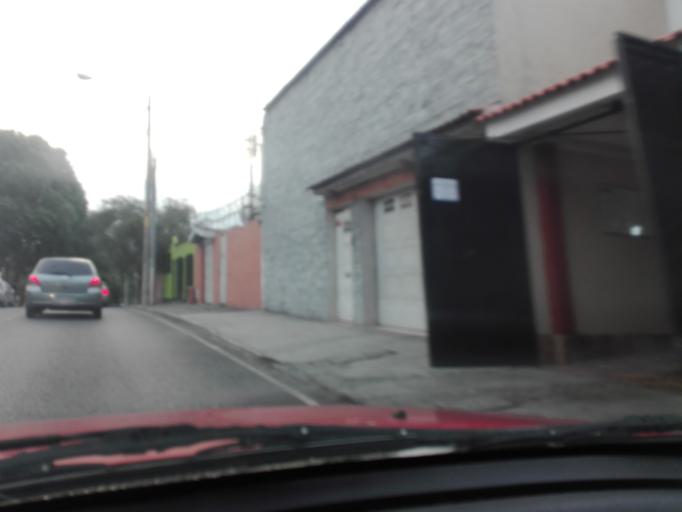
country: GT
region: Guatemala
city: Guatemala City
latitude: 14.6430
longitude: -90.5539
